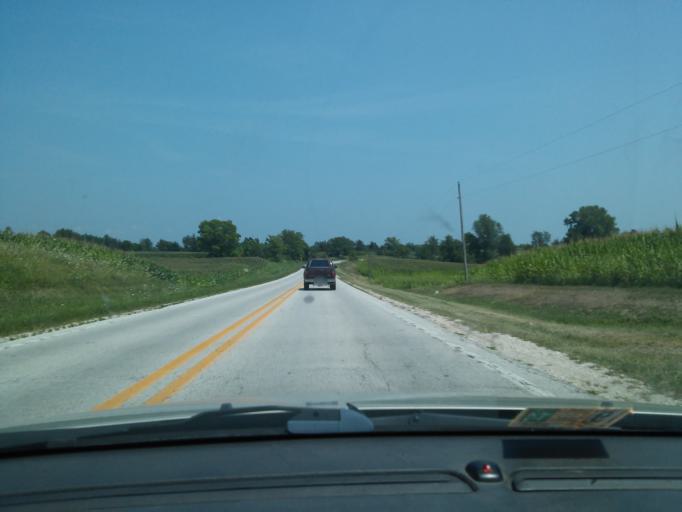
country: US
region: Illinois
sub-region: Pike County
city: Pittsfield
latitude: 39.5890
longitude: -90.8987
